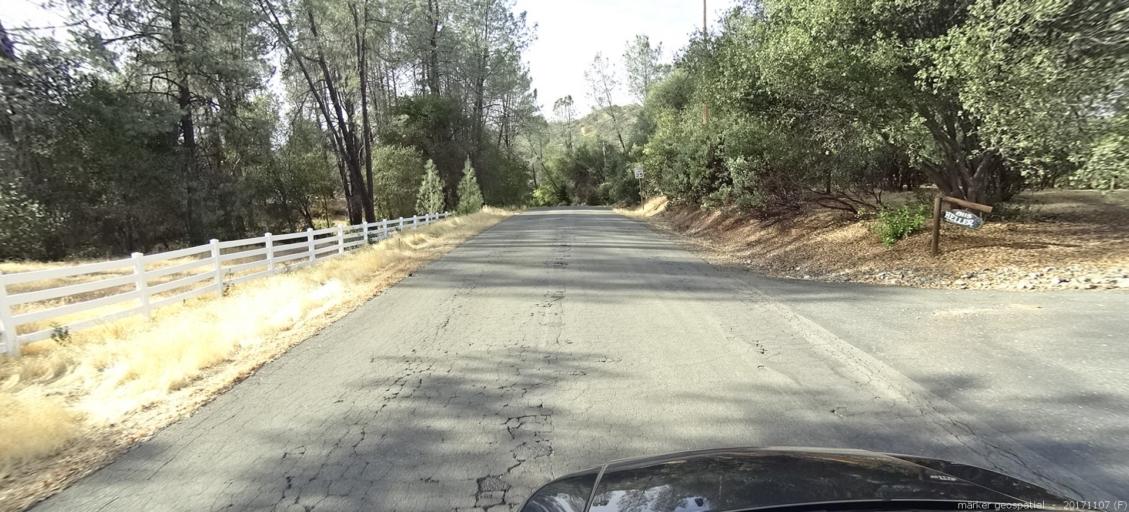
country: US
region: California
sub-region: Shasta County
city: Shasta
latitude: 40.5218
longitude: -122.4928
